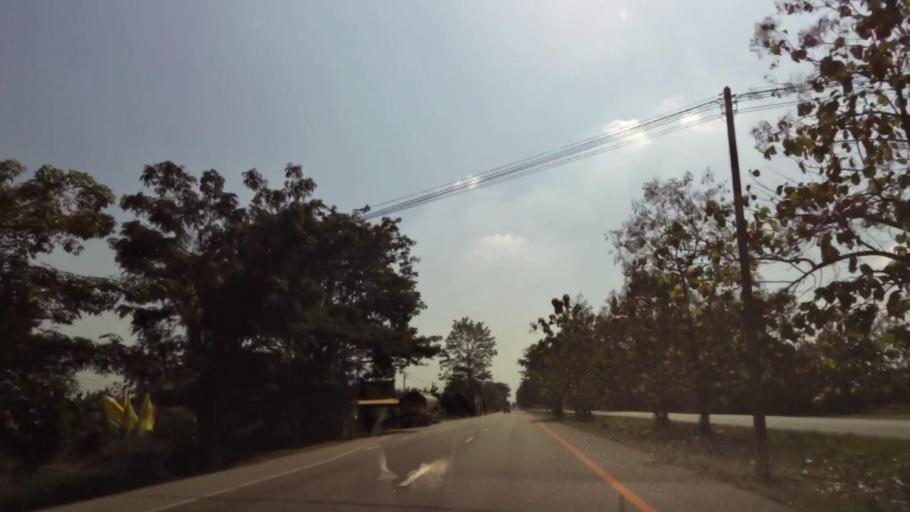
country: TH
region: Phichit
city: Bueng Na Rang
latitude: 16.2327
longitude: 100.1257
